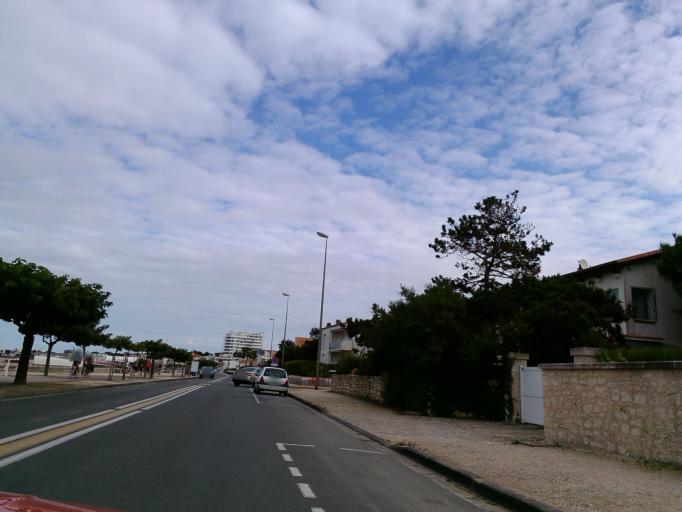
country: FR
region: Poitou-Charentes
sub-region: Departement de la Charente-Maritime
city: Saint-Georges-de-Didonne
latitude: 45.6091
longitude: -1.0086
